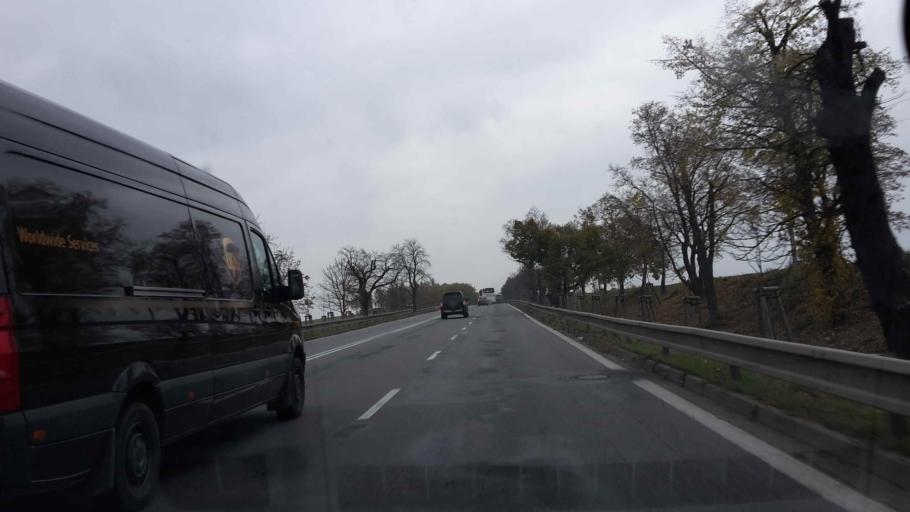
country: CZ
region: South Moravian
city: Slavkov u Brna
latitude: 49.1575
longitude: 16.8609
